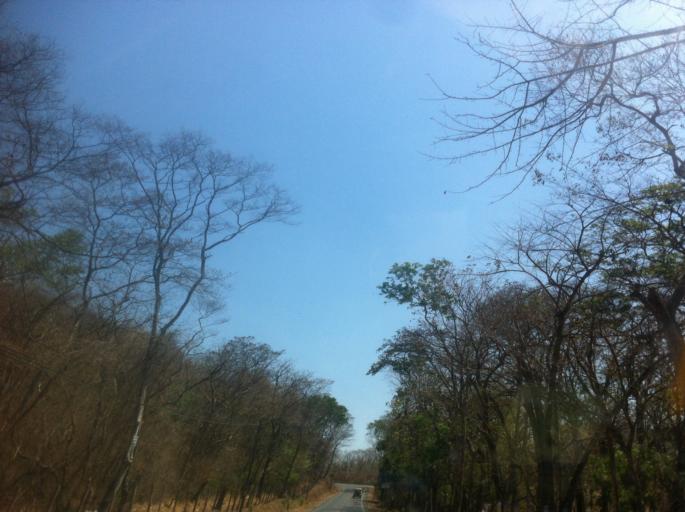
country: CR
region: Guanacaste
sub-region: Canton de Nicoya
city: Nicoya
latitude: 10.1229
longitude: -85.4460
